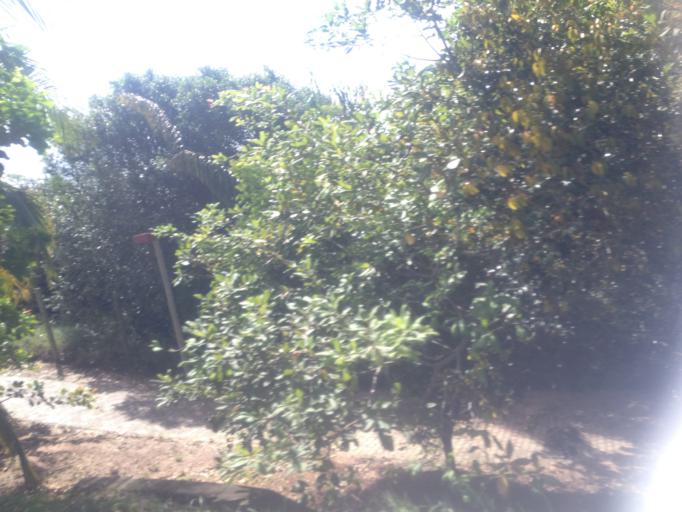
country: BR
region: Bahia
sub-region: Mata De Sao Joao
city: Mata de Sao Joao
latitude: -12.5713
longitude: -38.0145
